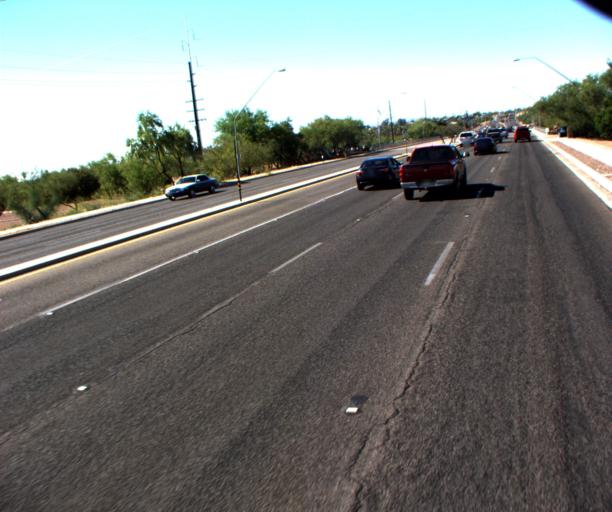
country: US
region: Arizona
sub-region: Pima County
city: Flowing Wells
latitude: 32.2928
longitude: -110.9781
